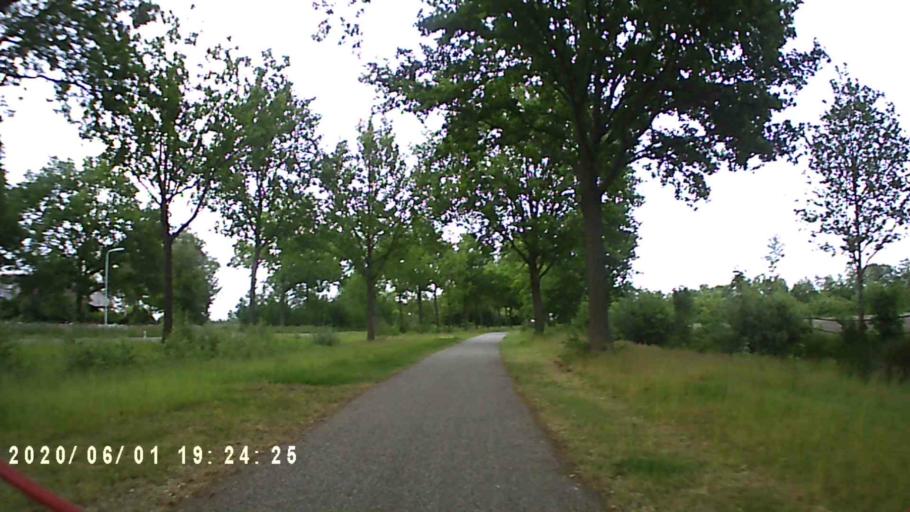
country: NL
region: Friesland
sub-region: Gemeente Achtkarspelen
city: Drogeham
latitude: 53.2059
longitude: 6.1284
